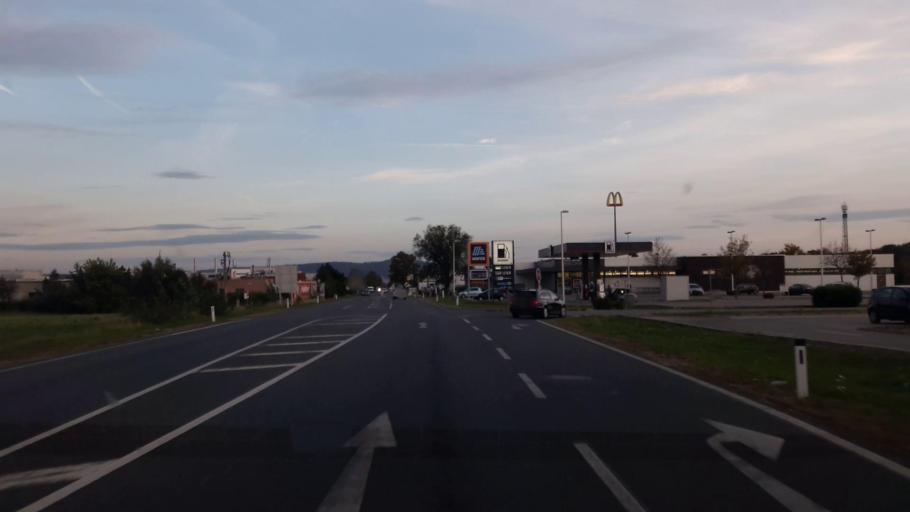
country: AT
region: Lower Austria
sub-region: Politischer Bezirk Korneuburg
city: Leobendorf
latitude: 48.3610
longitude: 16.3105
